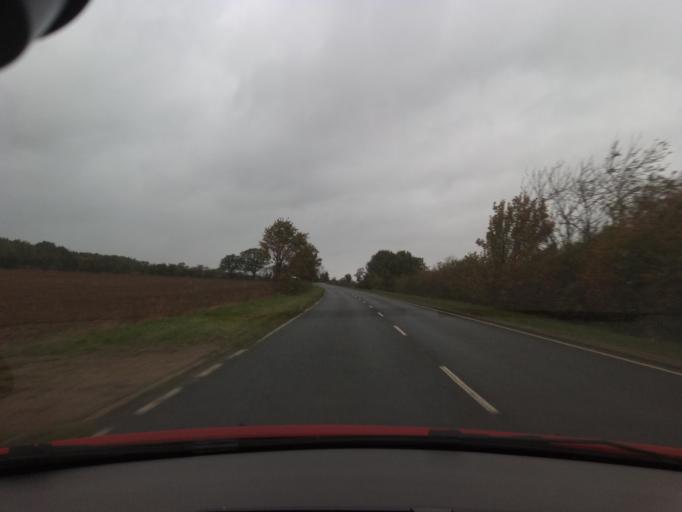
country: GB
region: England
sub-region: Essex
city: Great Yeldham
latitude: 52.0453
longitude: 0.5184
